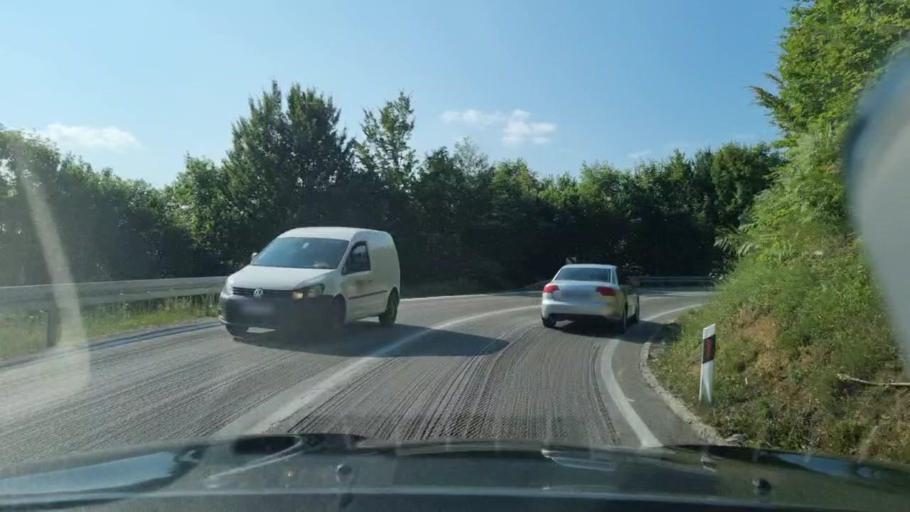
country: BA
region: Federation of Bosnia and Herzegovina
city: Skokovi
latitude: 45.0282
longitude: 15.9120
